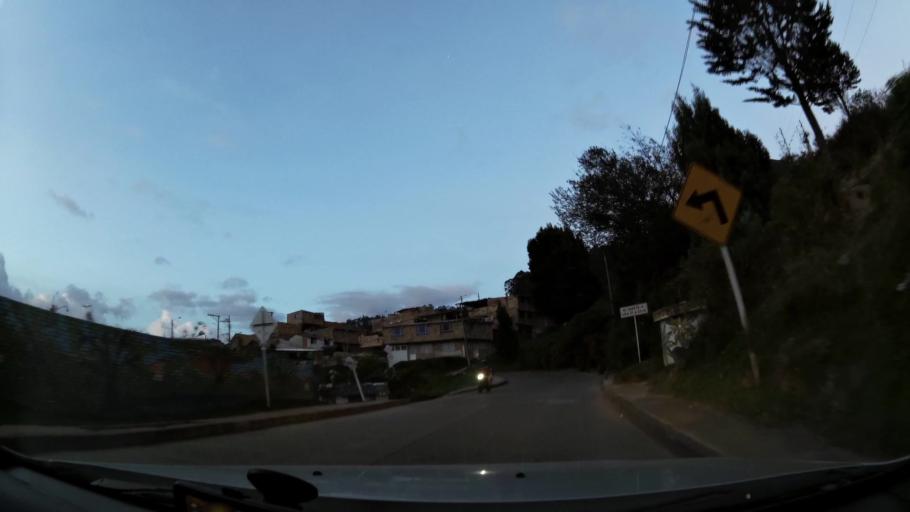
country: CO
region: Bogota D.C.
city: Bogota
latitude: 4.5427
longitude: -74.0799
